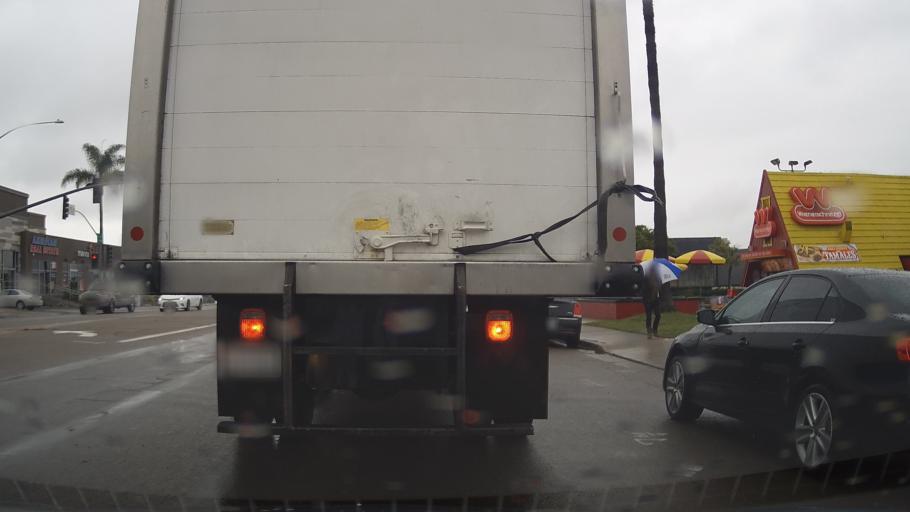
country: US
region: California
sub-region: San Diego County
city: San Diego
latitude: 32.8196
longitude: -117.1549
